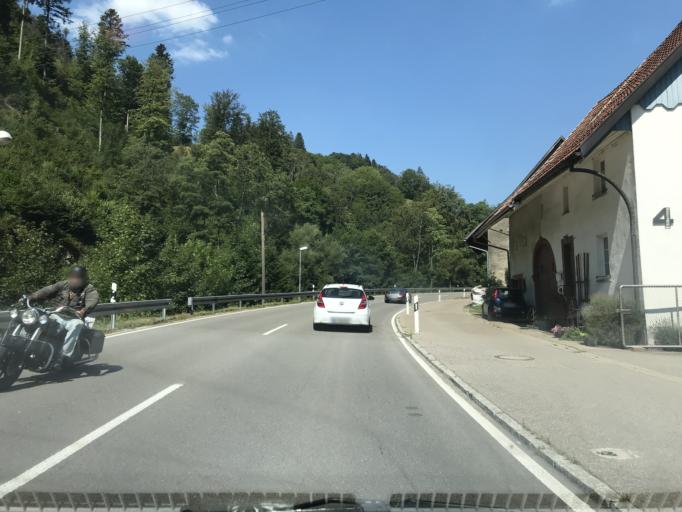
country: DE
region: Baden-Wuerttemberg
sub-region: Freiburg Region
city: Wembach
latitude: 47.7402
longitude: 7.8816
